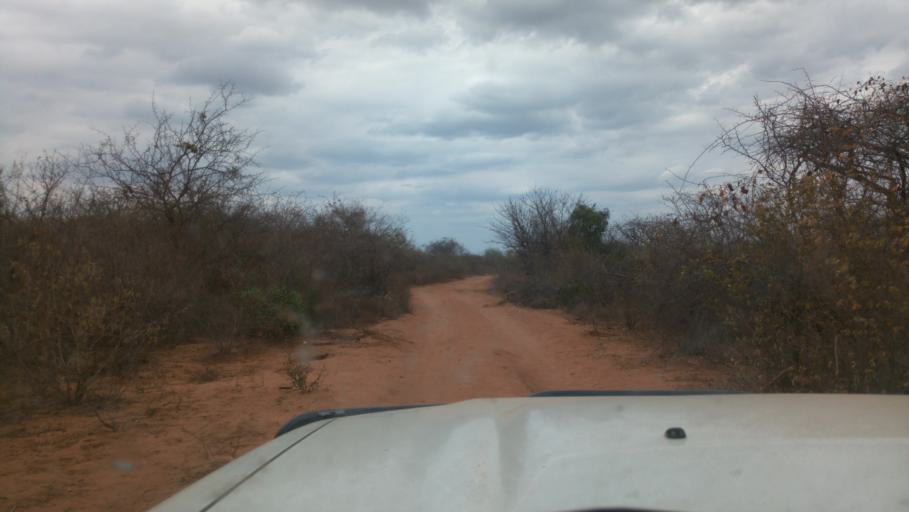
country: KE
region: Kitui
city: Kitui
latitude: -1.7783
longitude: 38.4476
